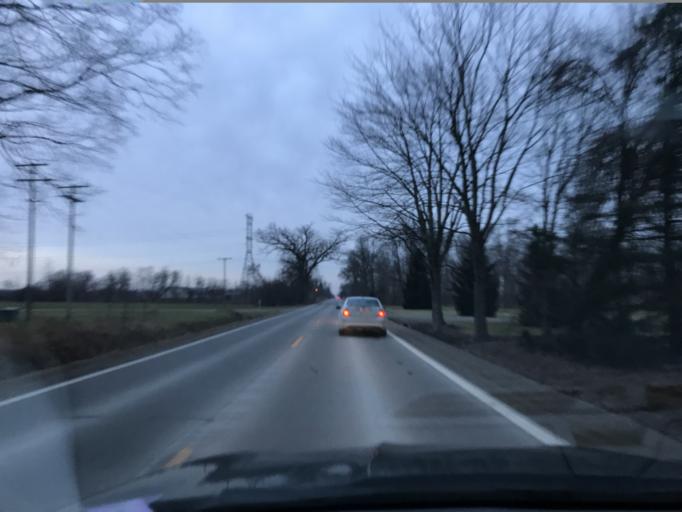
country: US
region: Michigan
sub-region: Macomb County
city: Romeo
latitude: 42.8296
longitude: -82.9636
